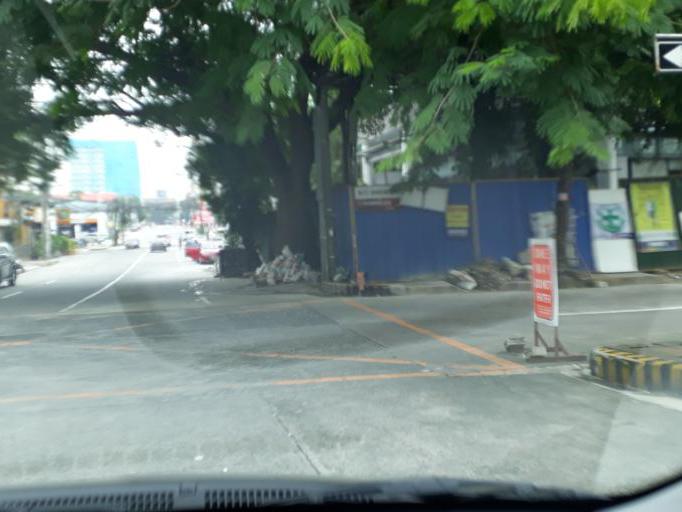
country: PH
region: Calabarzon
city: Del Monte
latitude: 14.6343
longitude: 121.0330
